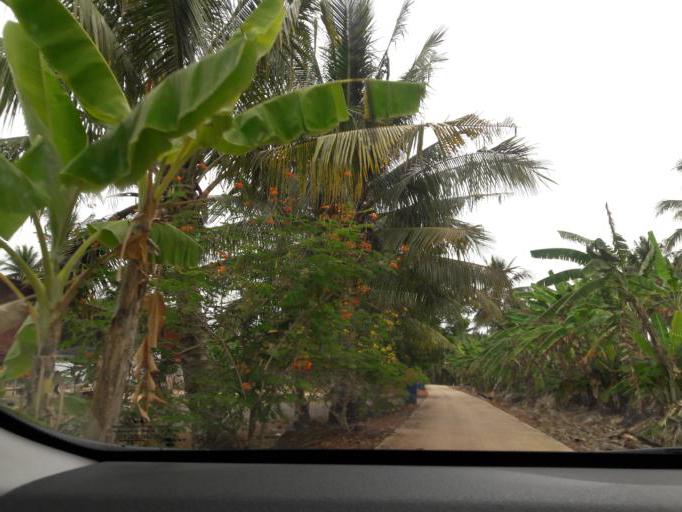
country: TH
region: Ratchaburi
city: Damnoen Saduak
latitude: 13.5692
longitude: 99.9777
